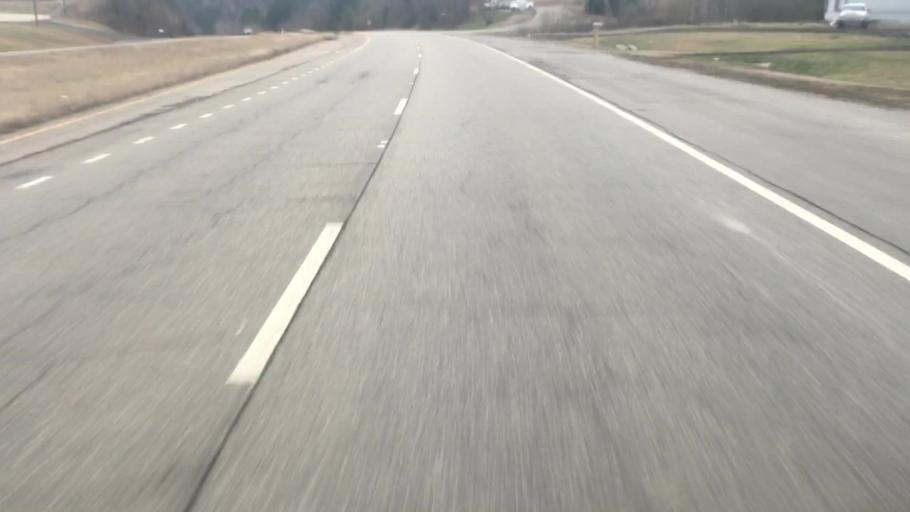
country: US
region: Alabama
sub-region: Walker County
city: Dora
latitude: 33.7956
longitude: -87.1091
